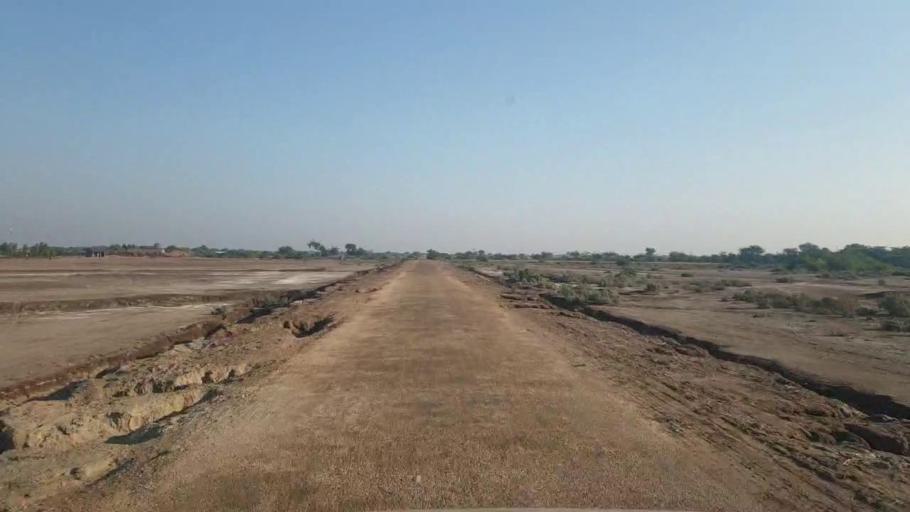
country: PK
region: Sindh
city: Badin
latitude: 24.7223
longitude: 68.8627
